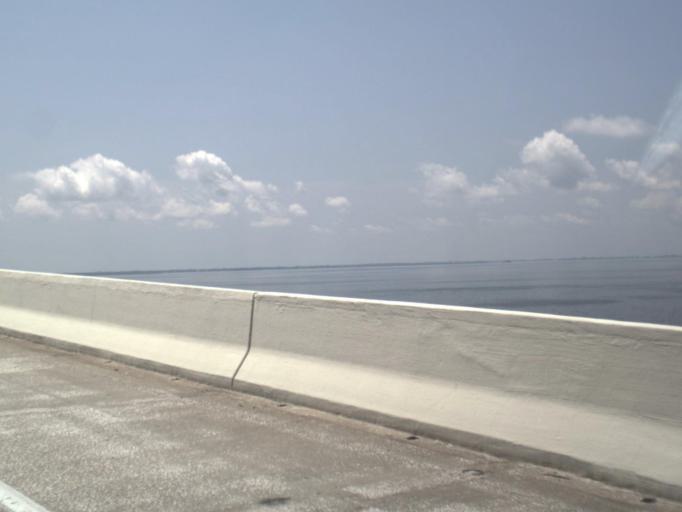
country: US
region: Florida
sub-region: Pinellas County
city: Tierra Verde
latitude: 27.6227
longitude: -82.6573
